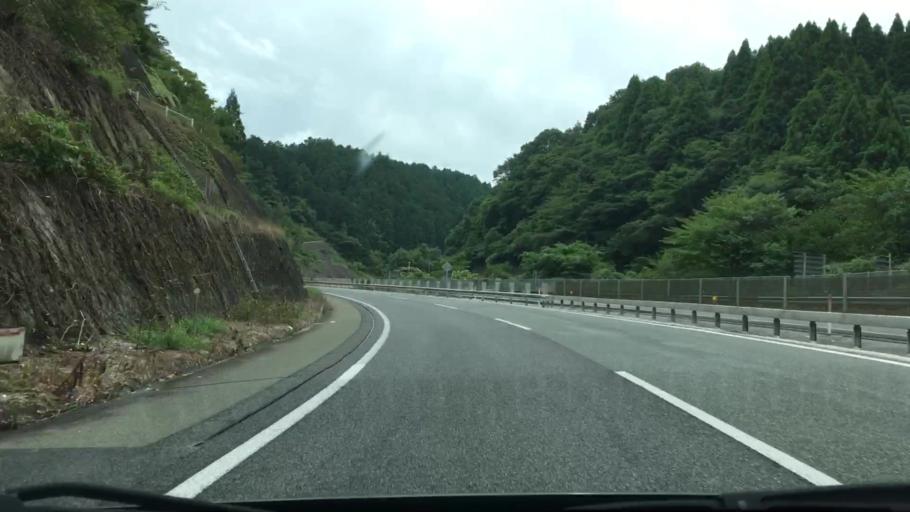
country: JP
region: Hiroshima
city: Shobara
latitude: 34.8946
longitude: 133.2258
